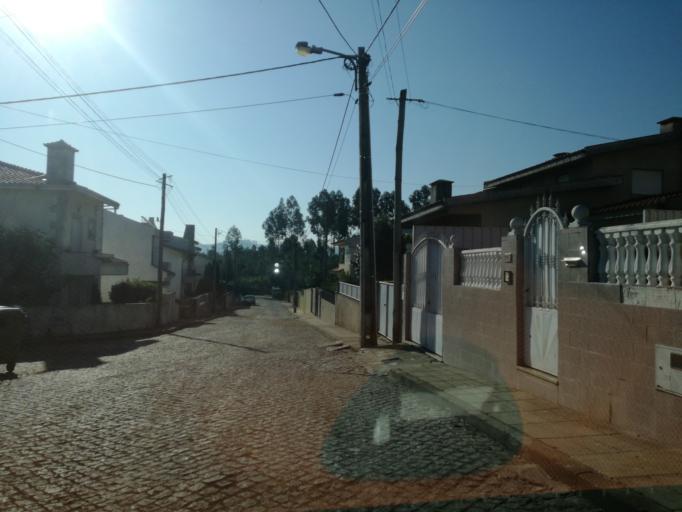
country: PT
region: Porto
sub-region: Trofa
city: Sao Romao do Coronado
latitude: 41.2624
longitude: -8.5706
